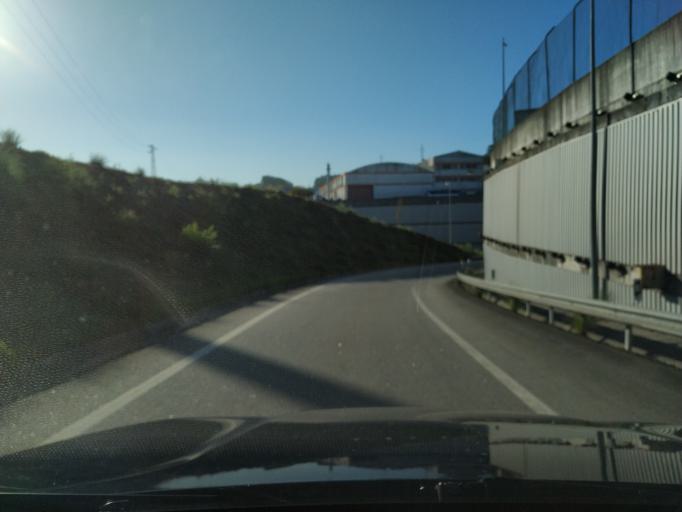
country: PT
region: Porto
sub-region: Vila Nova de Gaia
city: Vilar de Andorinho
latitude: 41.0946
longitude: -8.5905
